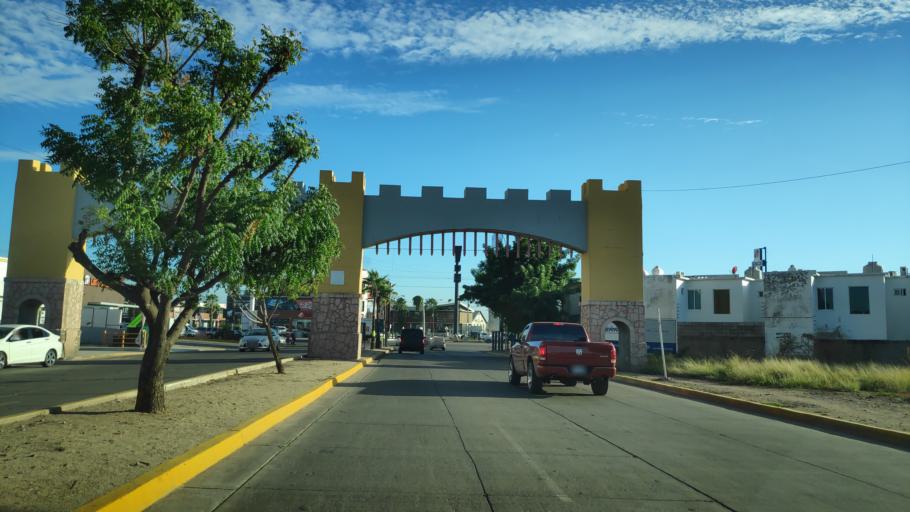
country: MX
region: Sinaloa
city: Culiacan
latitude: 24.8118
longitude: -107.4401
